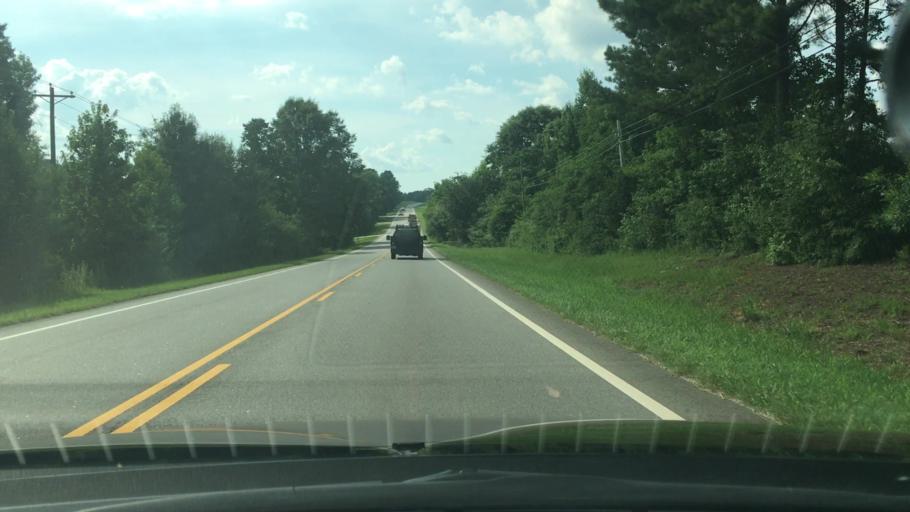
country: US
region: Georgia
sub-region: Coweta County
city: Senoia
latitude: 33.2694
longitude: -84.5253
